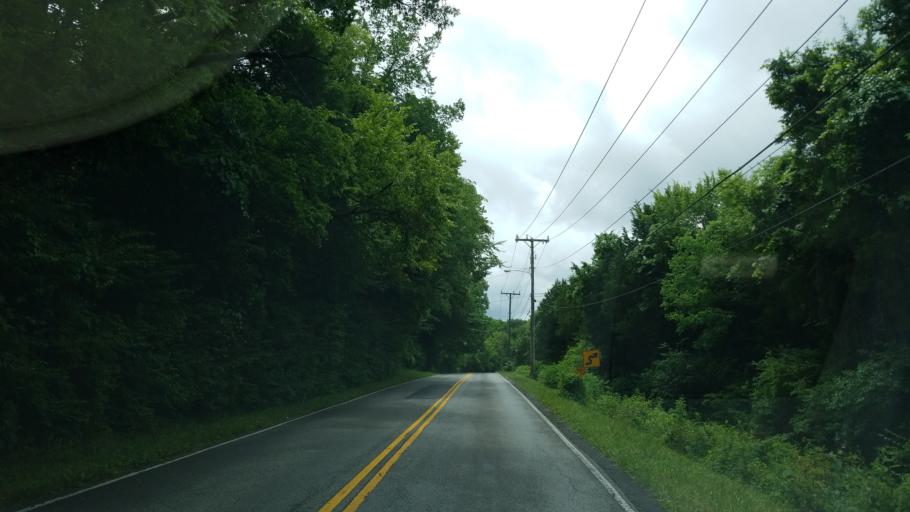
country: US
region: Tennessee
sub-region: Rutherford County
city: La Vergne
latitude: 36.0563
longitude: -86.6686
